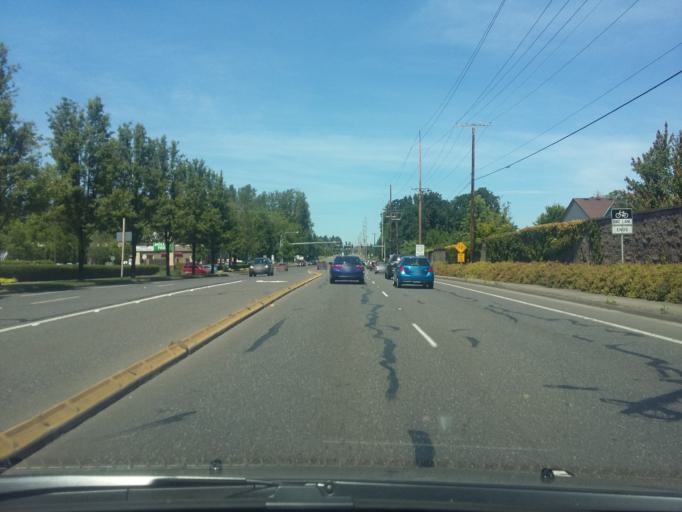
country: US
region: Washington
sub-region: Clark County
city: Mill Plain
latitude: 45.6701
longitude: -122.5059
